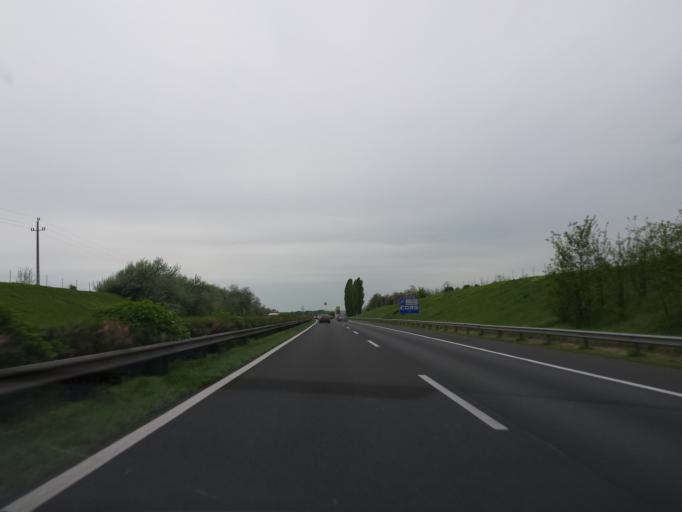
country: HU
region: Pest
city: Zsambek
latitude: 47.5103
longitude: 18.7438
